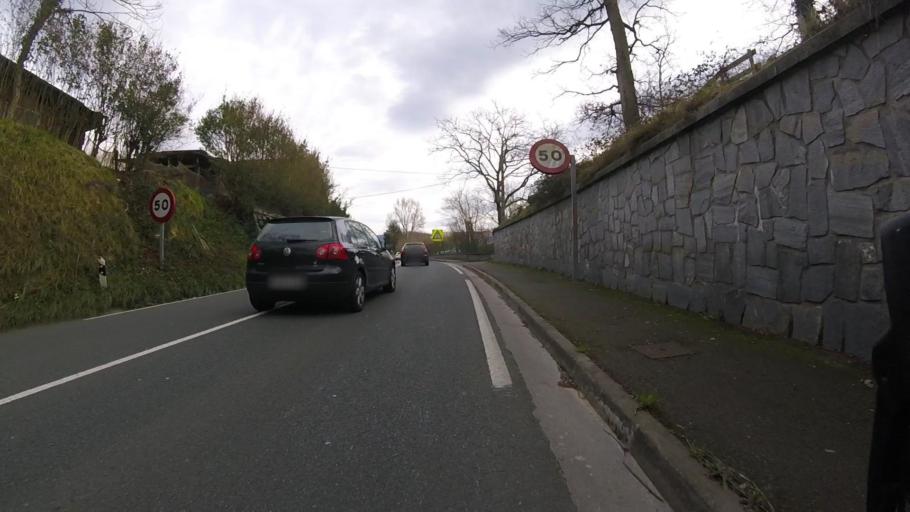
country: ES
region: Basque Country
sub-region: Provincia de Guipuzcoa
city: Lezo
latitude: 43.3042
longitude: -1.8755
